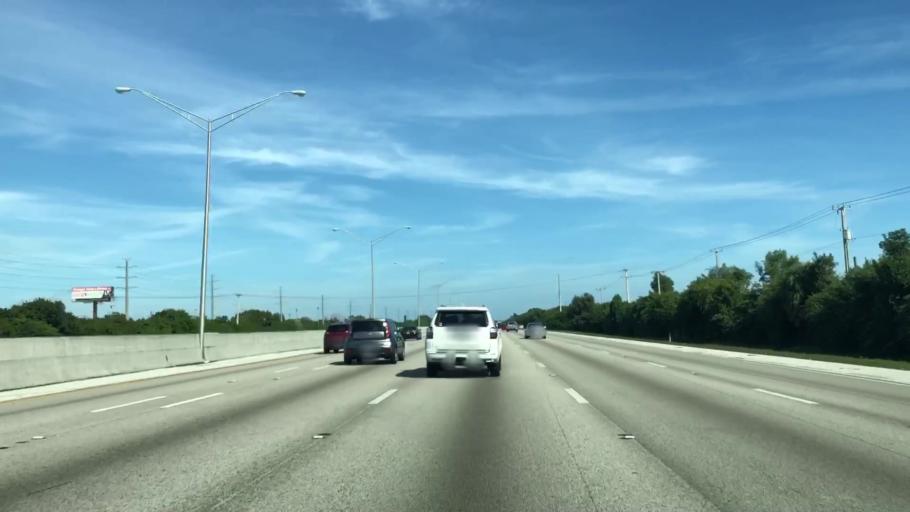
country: US
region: Florida
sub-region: Palm Beach County
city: Delray Beach
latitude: 26.4872
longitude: -80.0826
